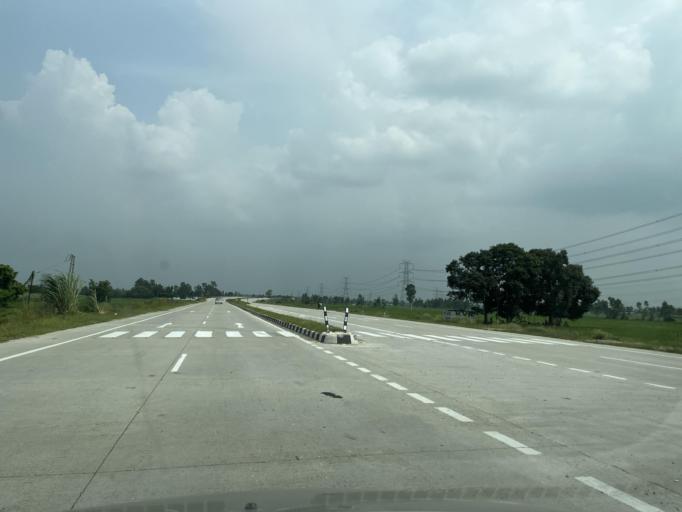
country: IN
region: Uttarakhand
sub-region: Udham Singh Nagar
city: Jaspur
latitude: 29.2916
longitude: 78.8488
